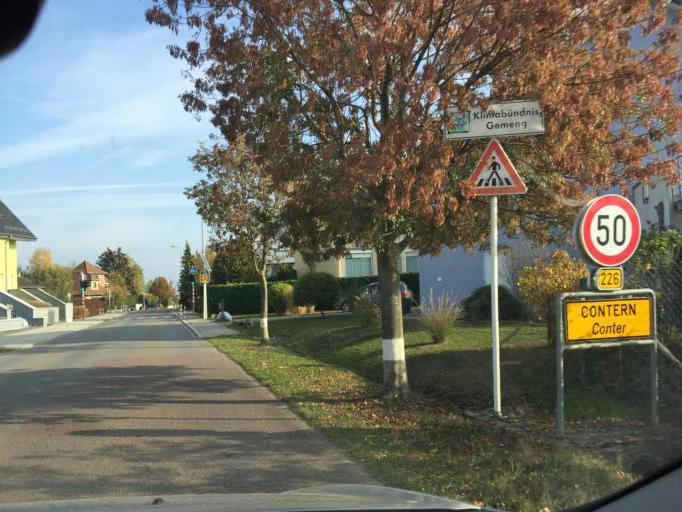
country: LU
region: Luxembourg
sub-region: Canton de Luxembourg
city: Contern
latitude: 49.5784
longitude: 6.2226
